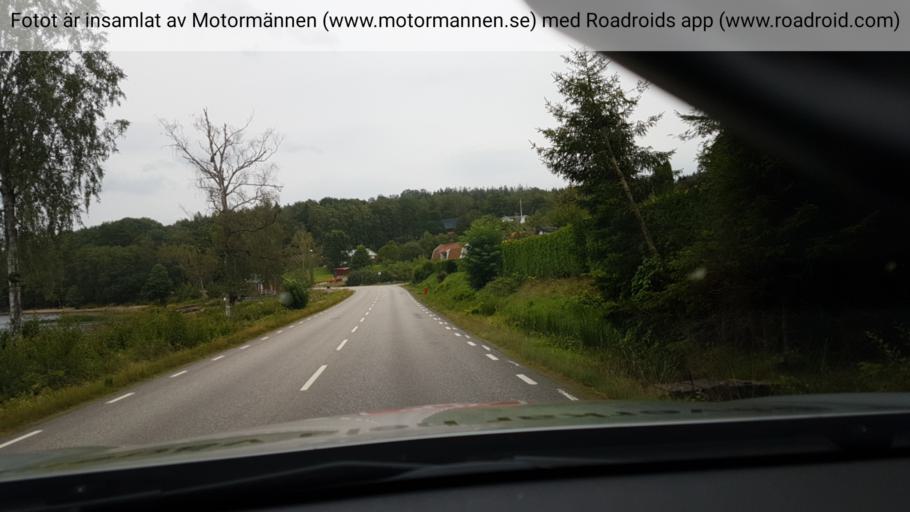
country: SE
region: Vaestra Goetaland
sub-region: Harryda Kommun
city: Hindas
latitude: 57.6096
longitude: 12.3804
